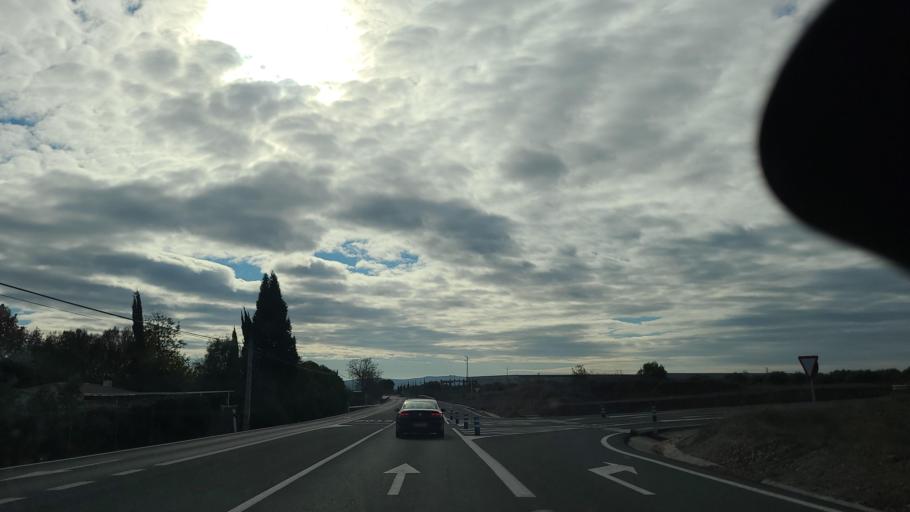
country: ES
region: Andalusia
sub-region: Provincia de Jaen
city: Villanueva de la Reina
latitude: 38.0432
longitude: -3.9122
